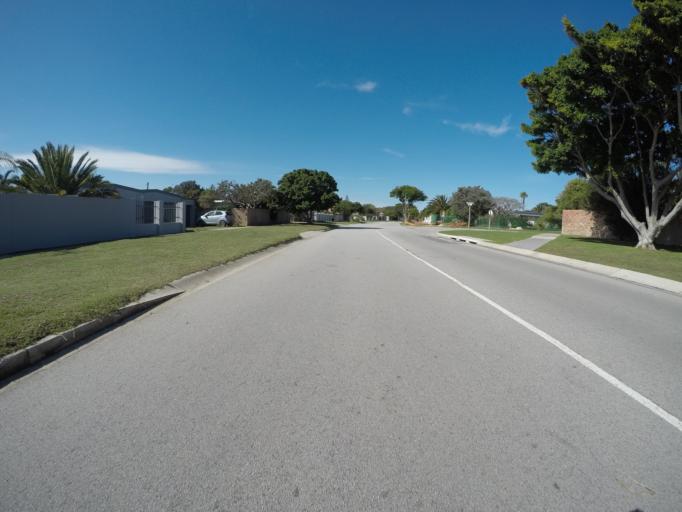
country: ZA
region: Eastern Cape
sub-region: Nelson Mandela Bay Metropolitan Municipality
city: Port Elizabeth
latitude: -33.9933
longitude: 25.6621
